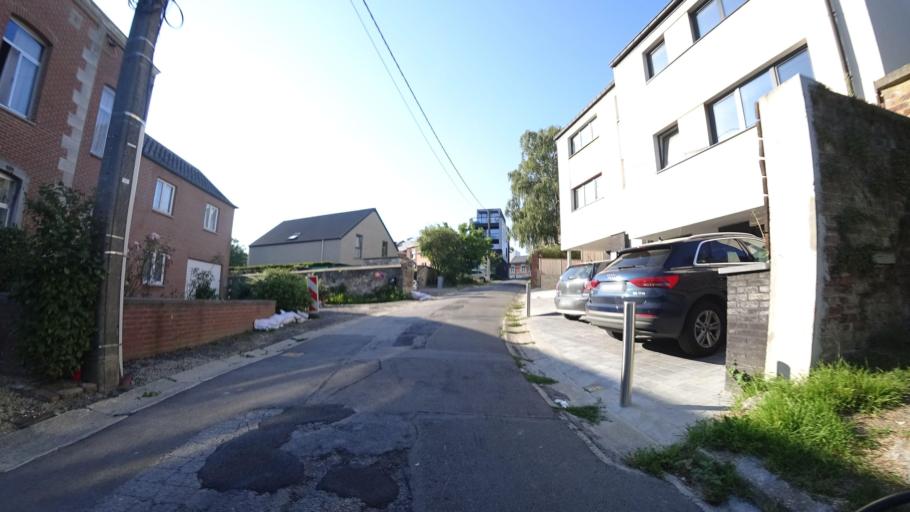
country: BE
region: Wallonia
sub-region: Province de Namur
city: Namur
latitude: 50.4718
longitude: 4.8303
